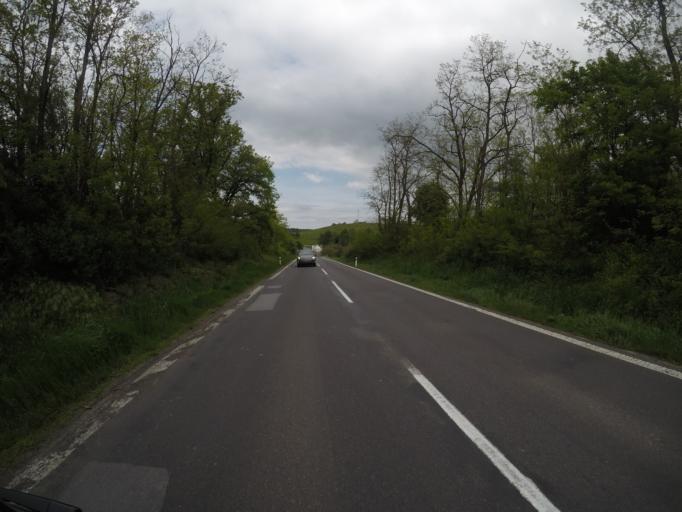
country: SK
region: Banskobystricky
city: Krupina
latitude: 48.3012
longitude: 19.0248
